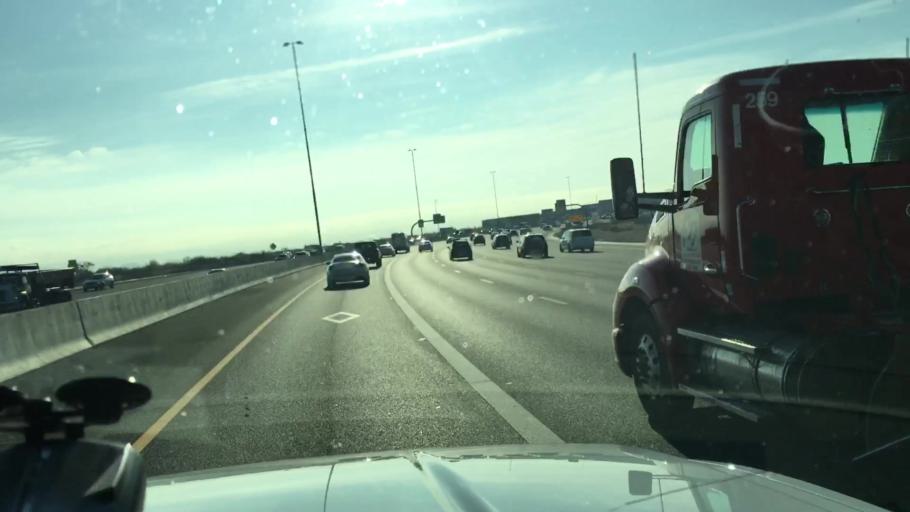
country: US
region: Arizona
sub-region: Maricopa County
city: Scottsdale
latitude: 33.5609
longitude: -111.8830
